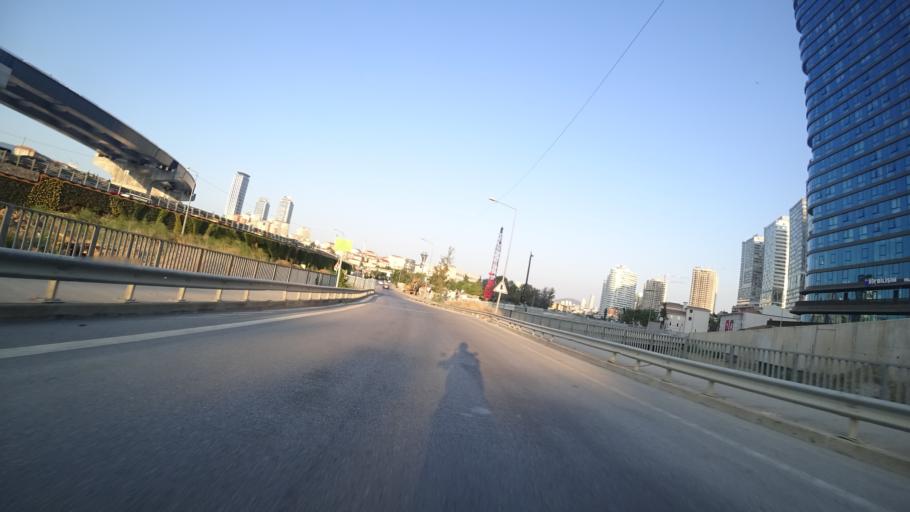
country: TR
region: Istanbul
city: UEskuedar
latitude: 40.9965
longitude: 29.0566
